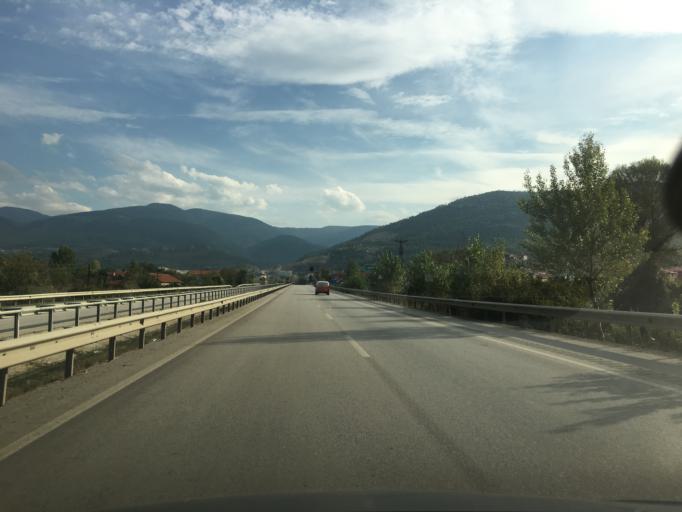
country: TR
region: Karabuk
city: Karabuk
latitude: 41.1078
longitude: 32.6686
